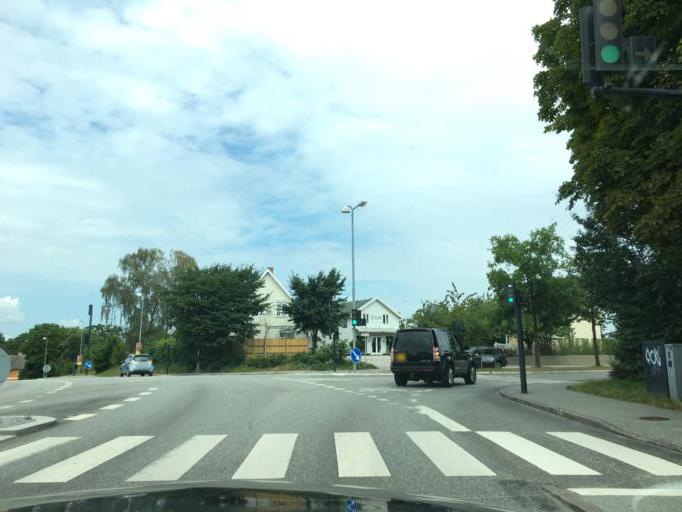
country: DK
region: Capital Region
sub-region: Horsholm Kommune
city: Horsholm
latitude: 55.8917
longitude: 12.4960
